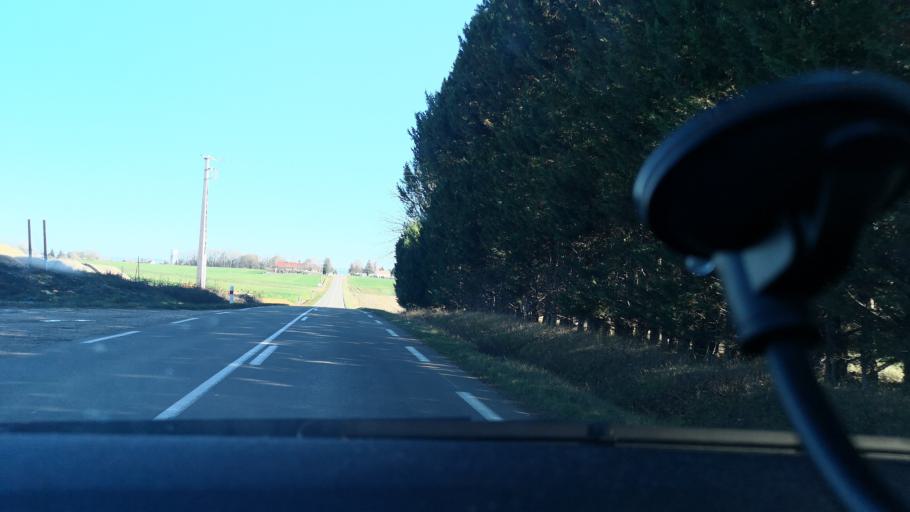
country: FR
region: Franche-Comte
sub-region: Departement du Jura
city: Bletterans
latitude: 46.7446
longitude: 5.4277
